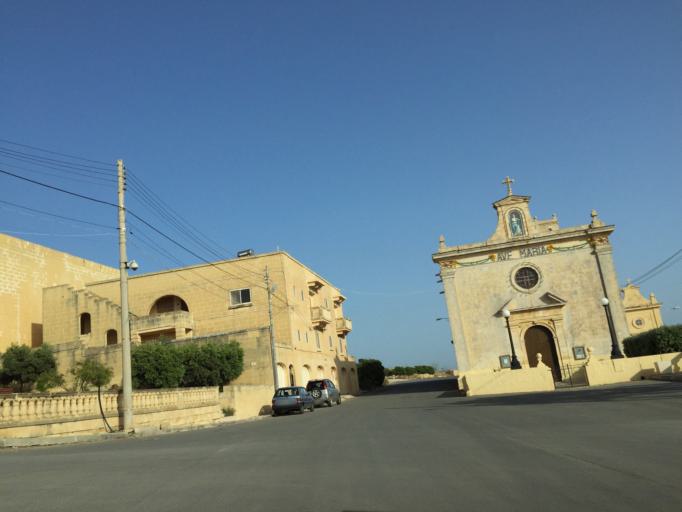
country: MT
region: Il-Qala
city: Qala
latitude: 36.0345
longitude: 14.3207
